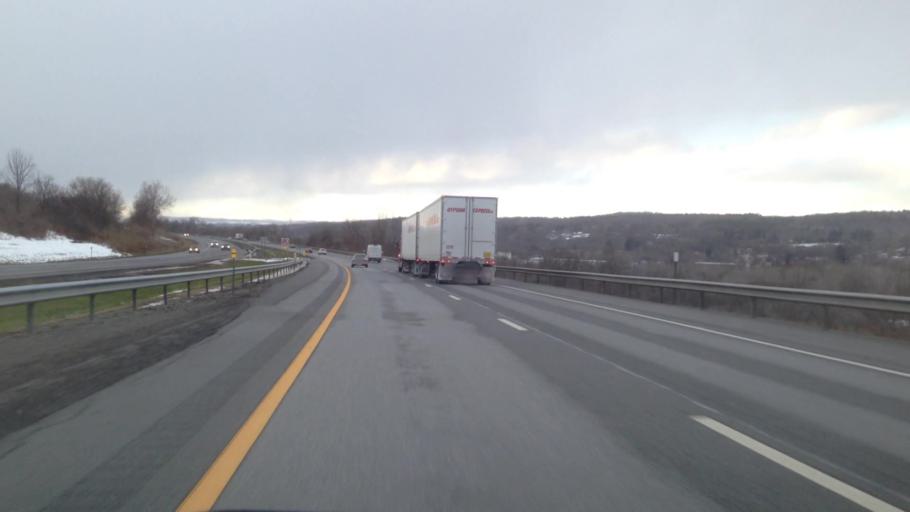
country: US
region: New York
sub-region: Montgomery County
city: Saint Johnsville
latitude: 42.9869
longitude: -74.6660
